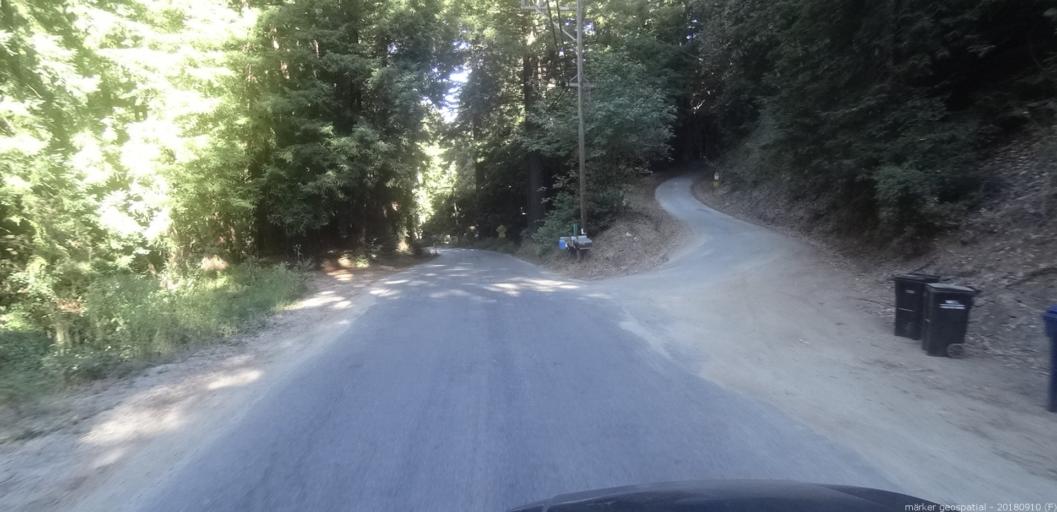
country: US
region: California
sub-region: Monterey County
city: Carmel Valley Village
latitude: 36.3913
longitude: -121.8751
